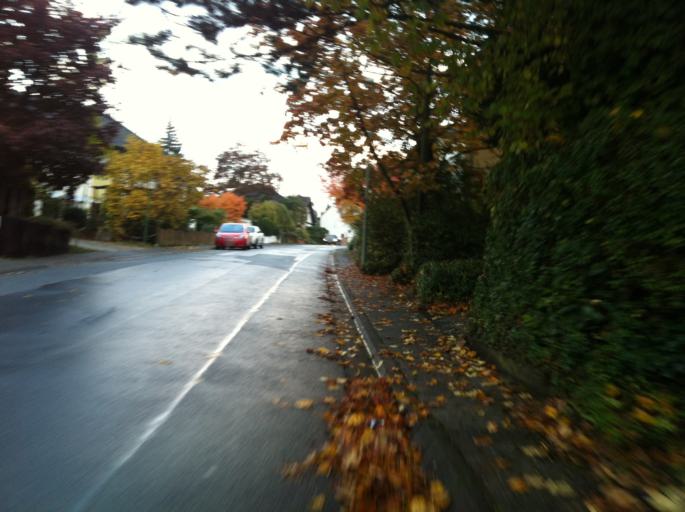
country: DE
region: Rheinland-Pfalz
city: Wackernheim
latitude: 49.9779
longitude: 8.1210
